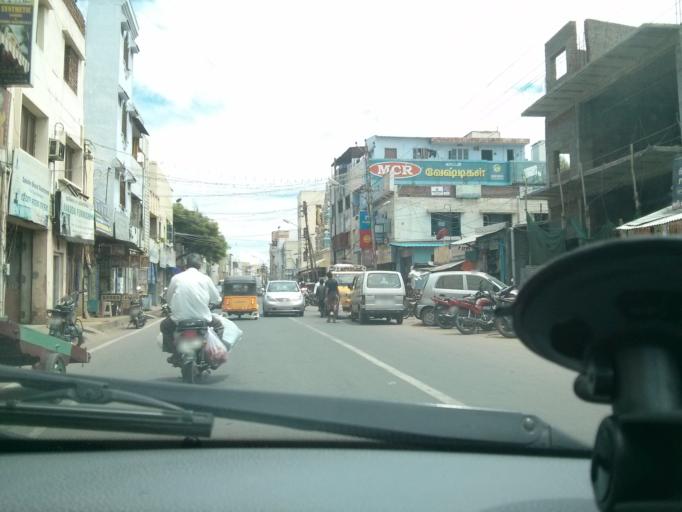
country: IN
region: Tamil Nadu
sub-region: Coimbatore
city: Coimbatore
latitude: 11.0020
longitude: 76.9564
